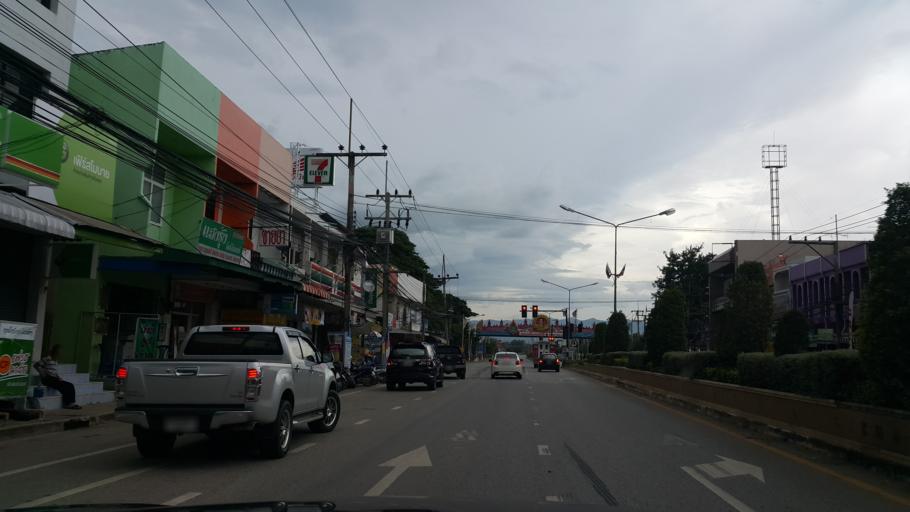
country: TH
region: Phayao
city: Dok Kham Tai
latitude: 19.1628
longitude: 99.9912
